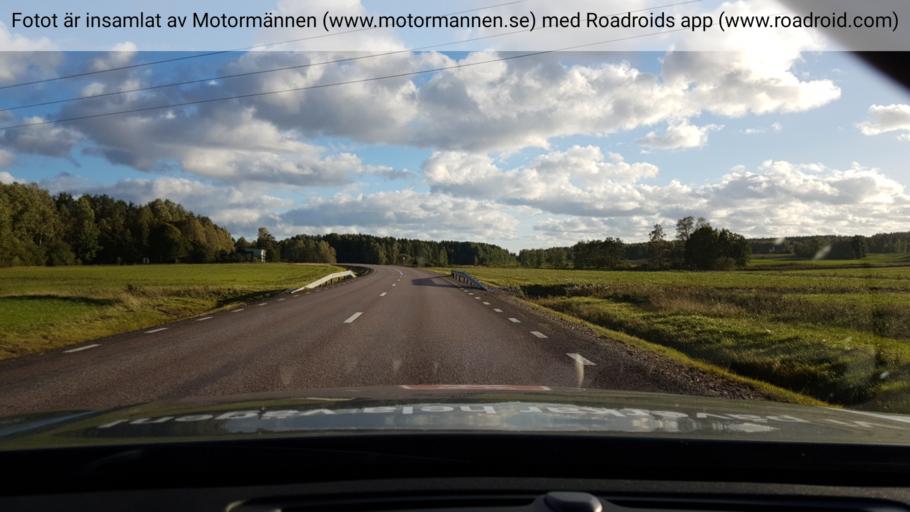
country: SE
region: Vaermland
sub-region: Karlstads Kommun
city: Molkom
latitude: 59.6202
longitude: 13.7294
